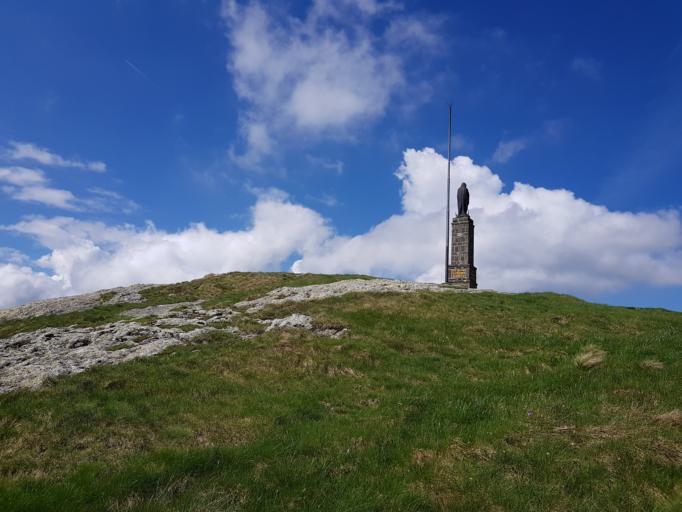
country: IT
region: Liguria
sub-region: Provincia di Genova
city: Santo Stefano d'Aveto
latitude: 44.5501
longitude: 9.4887
